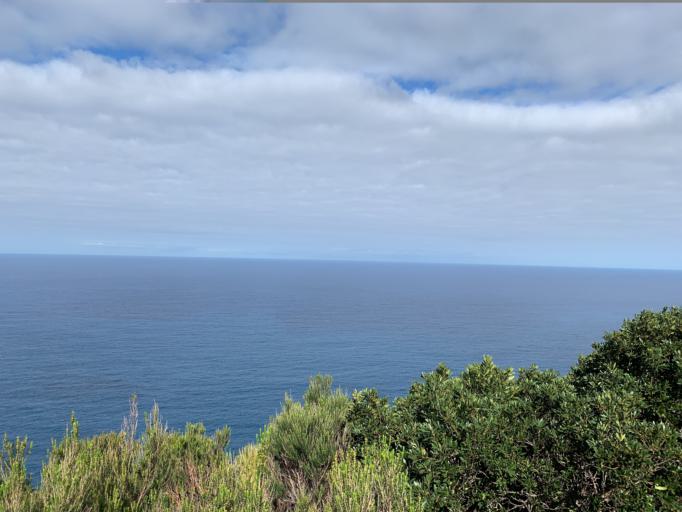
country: PT
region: Madeira
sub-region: Machico
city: Canical
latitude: 32.7556
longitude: -16.7724
